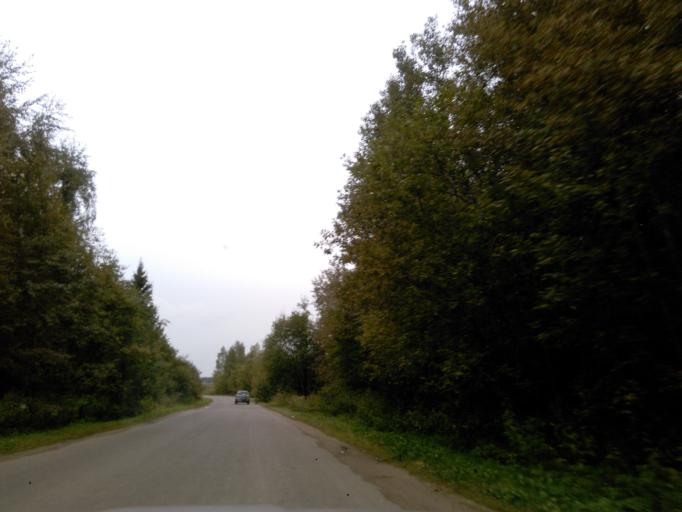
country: RU
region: Moskovskaya
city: Mendeleyevo
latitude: 56.1038
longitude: 37.2682
